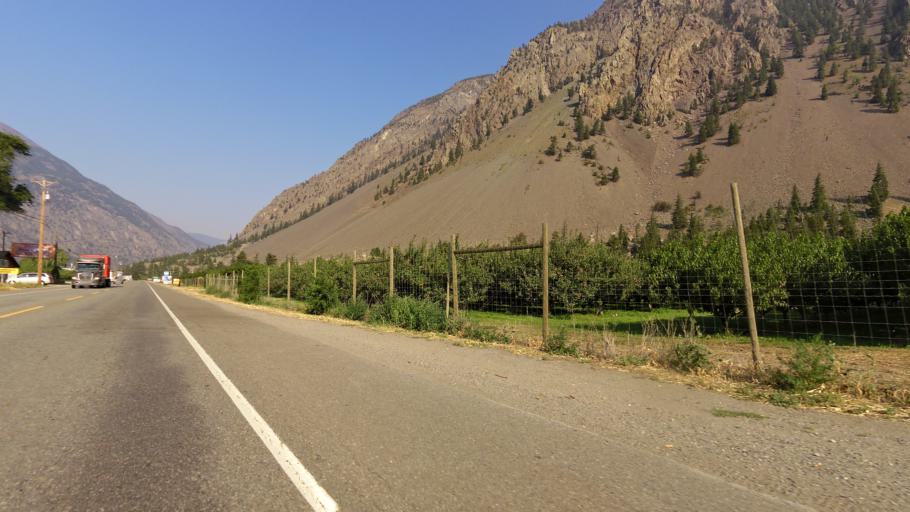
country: CA
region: British Columbia
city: Oliver
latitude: 49.2053
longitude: -119.8505
